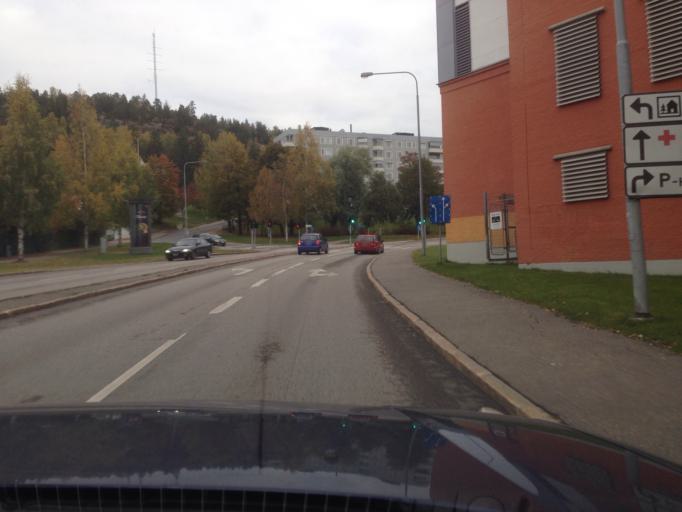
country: SE
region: Vaesternorrland
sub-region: Sundsvalls Kommun
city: Sundsvall
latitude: 62.3939
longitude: 17.3031
